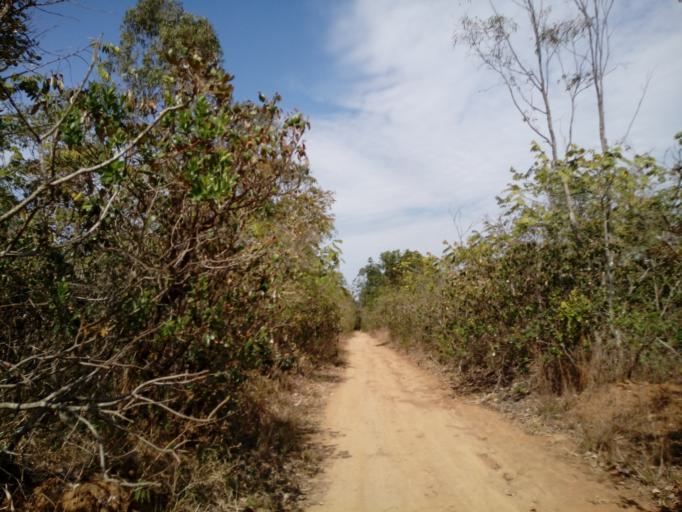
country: BR
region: Sao Paulo
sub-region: Sao Carlos
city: Sao Carlos
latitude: -21.9735
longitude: -47.8824
